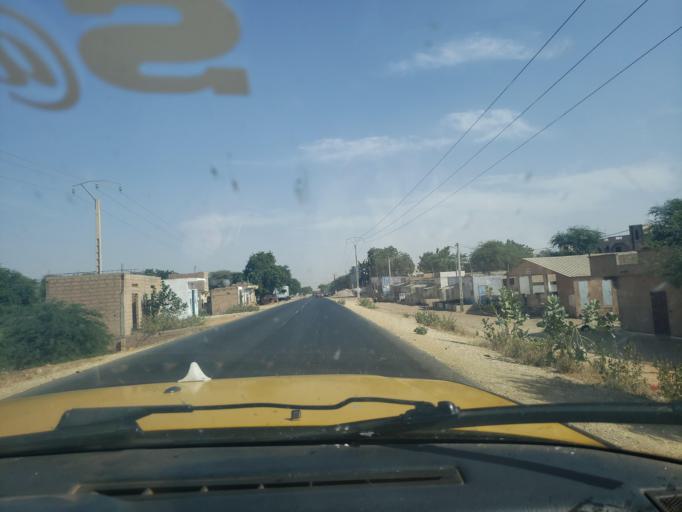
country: SN
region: Saint-Louis
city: Saint-Louis
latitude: 15.9292
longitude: -16.3263
